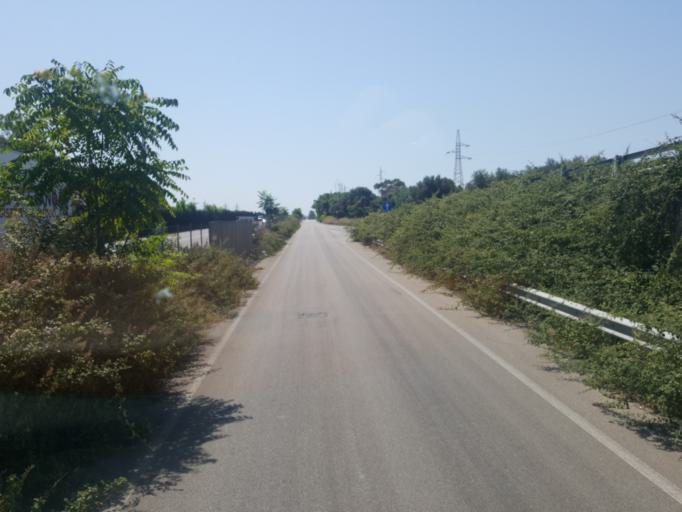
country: IT
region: Apulia
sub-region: Provincia di Taranto
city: Statte
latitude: 40.5094
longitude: 17.1928
